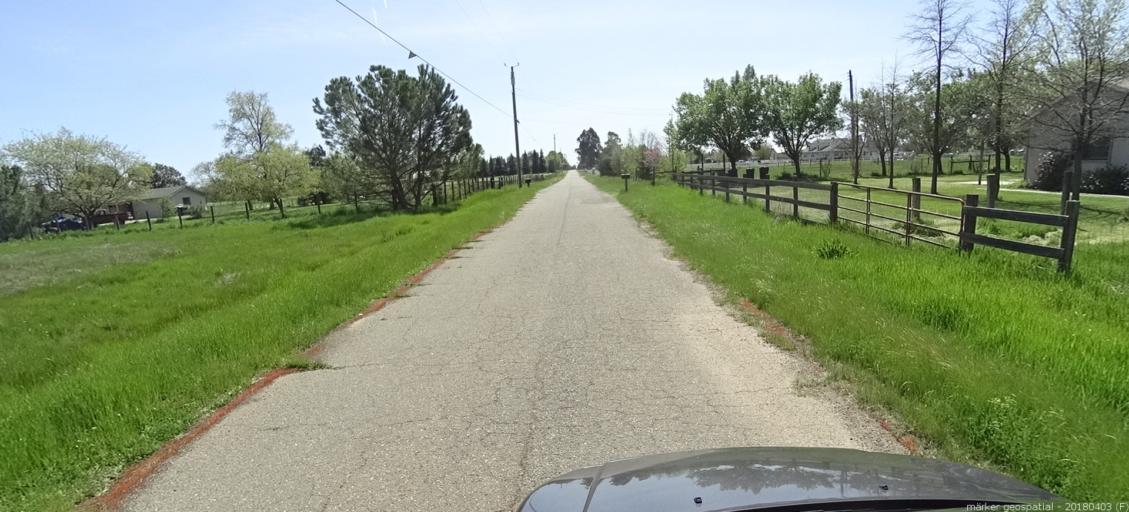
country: US
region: California
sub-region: Sacramento County
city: Wilton
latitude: 38.3919
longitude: -121.2469
